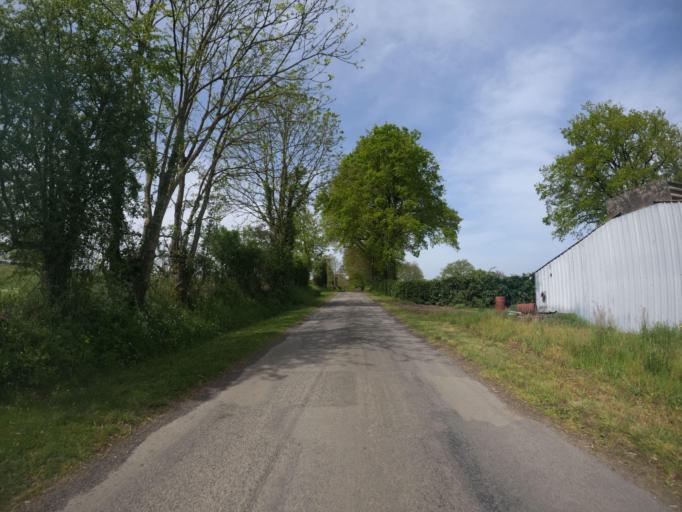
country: FR
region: Poitou-Charentes
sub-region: Departement des Deux-Sevres
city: La Chapelle-Saint-Laurent
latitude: 46.7107
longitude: -0.4988
